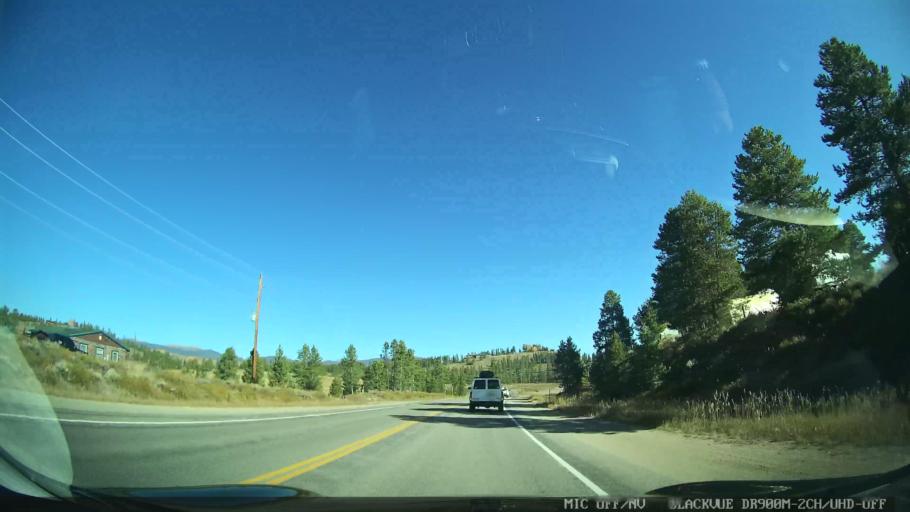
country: US
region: Colorado
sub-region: Grand County
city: Granby
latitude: 40.1721
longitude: -105.9008
